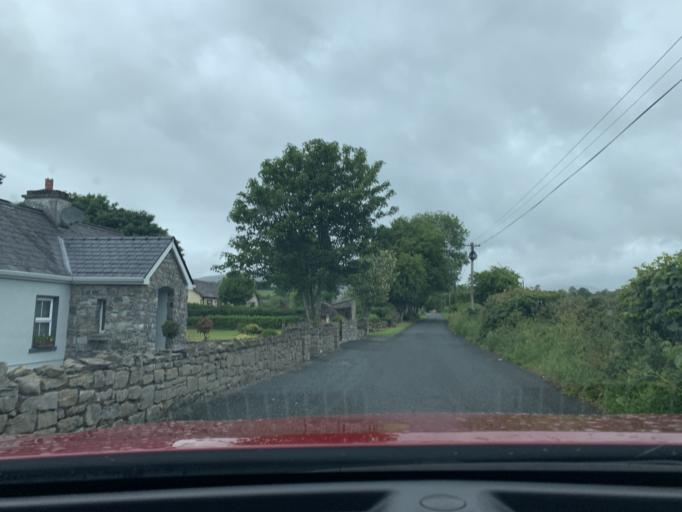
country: IE
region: Connaught
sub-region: Sligo
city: Sligo
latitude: 54.2995
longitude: -8.4589
